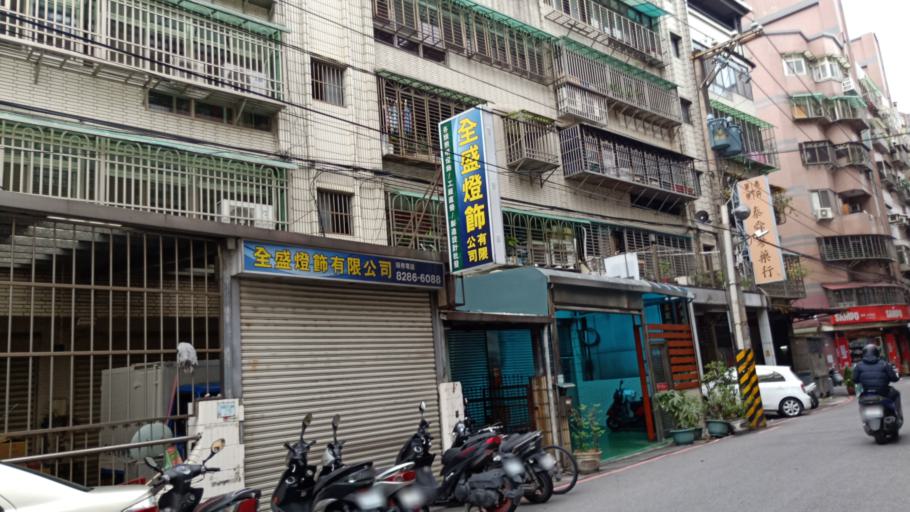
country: TW
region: Taipei
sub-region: Taipei
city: Banqiao
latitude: 25.0890
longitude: 121.4582
